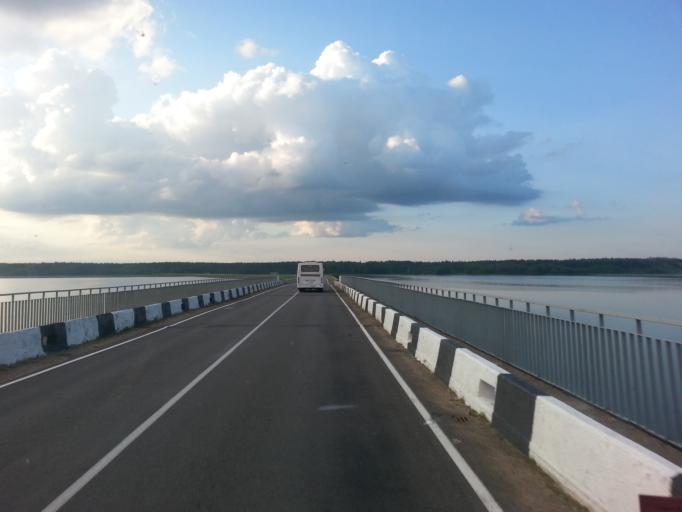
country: BY
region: Minsk
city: Il'ya
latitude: 54.5068
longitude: 27.2260
